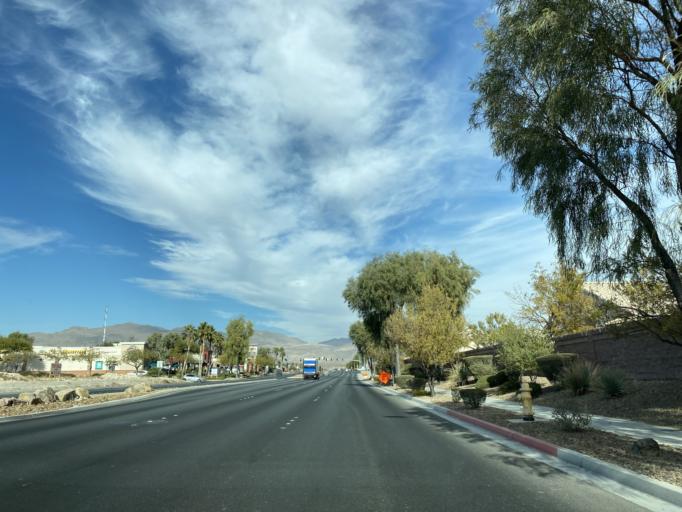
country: US
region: Nevada
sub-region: Clark County
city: Nellis Air Force Base
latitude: 36.2736
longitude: -115.1169
